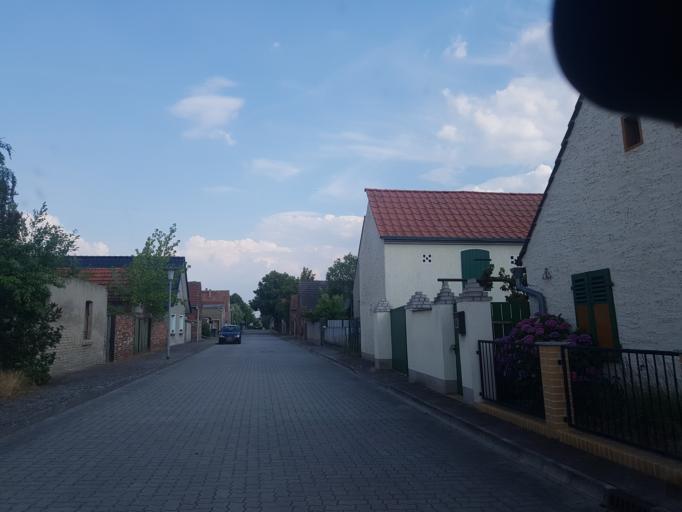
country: DE
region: Saxony-Anhalt
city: Holzdorf
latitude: 51.7768
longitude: 13.2132
